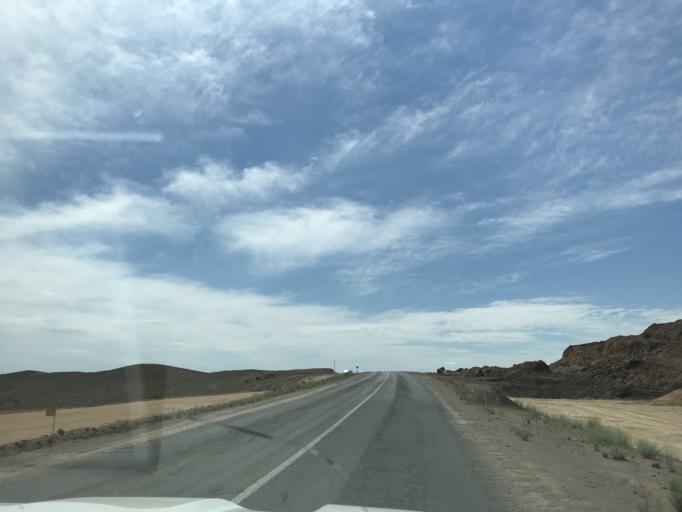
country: KZ
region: Almaty Oblysy
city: Ulken
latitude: 45.0830
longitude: 73.9704
